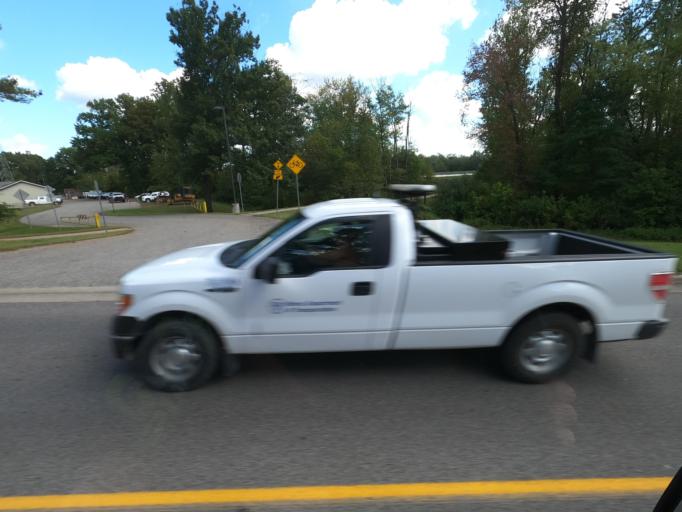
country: US
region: Illinois
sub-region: Johnson County
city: Vienna
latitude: 37.4200
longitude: -88.8932
